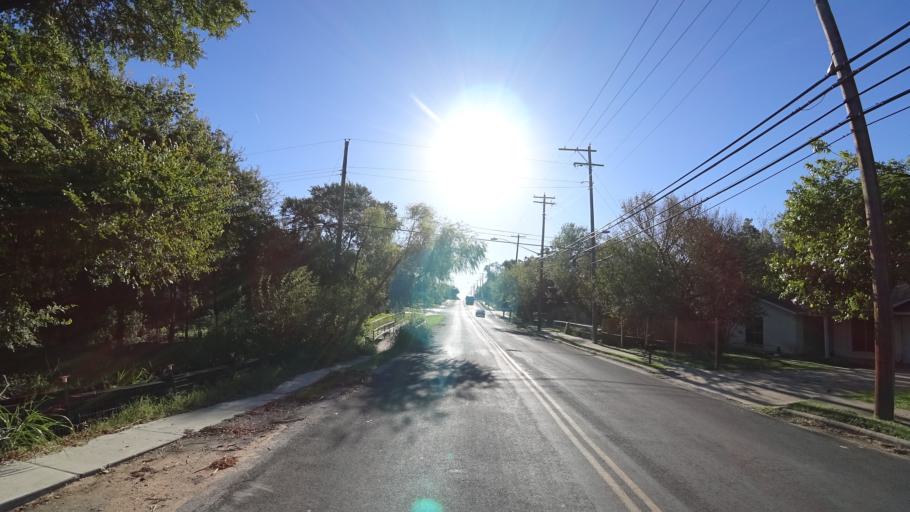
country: US
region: Texas
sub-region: Travis County
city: Austin
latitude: 30.3038
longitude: -97.6799
